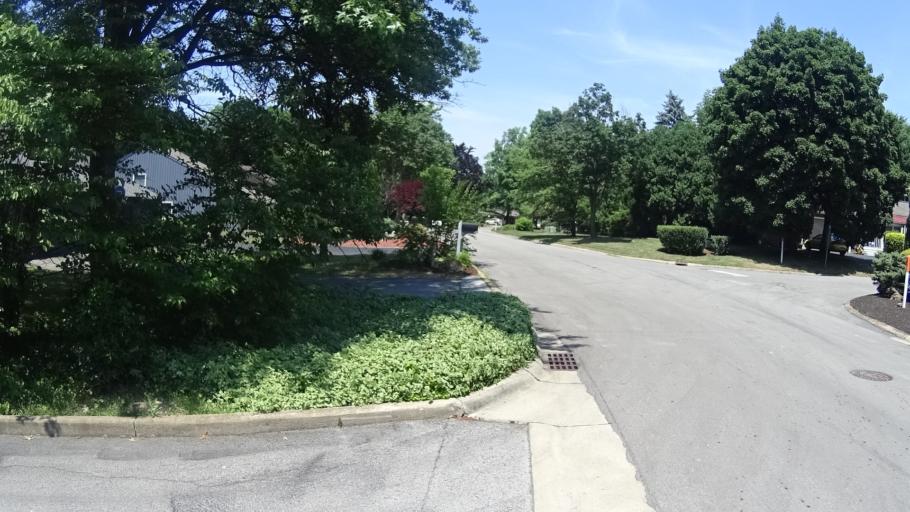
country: US
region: Ohio
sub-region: Erie County
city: Sandusky
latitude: 41.4072
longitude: -82.6416
